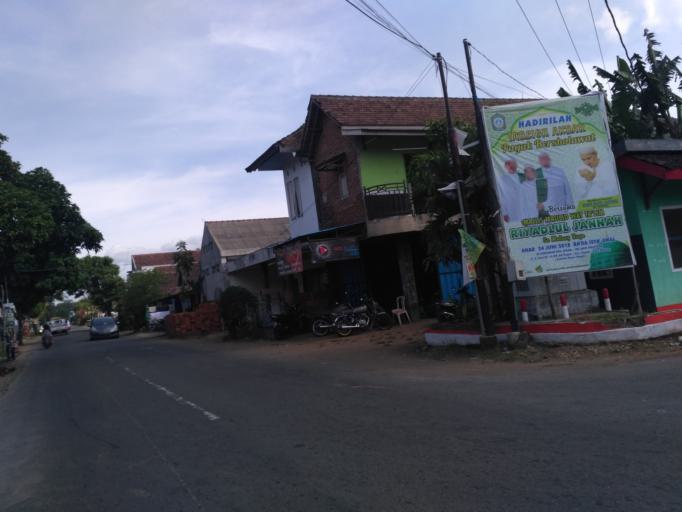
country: ID
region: East Java
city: Golek
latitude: -8.0637
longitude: 112.6266
